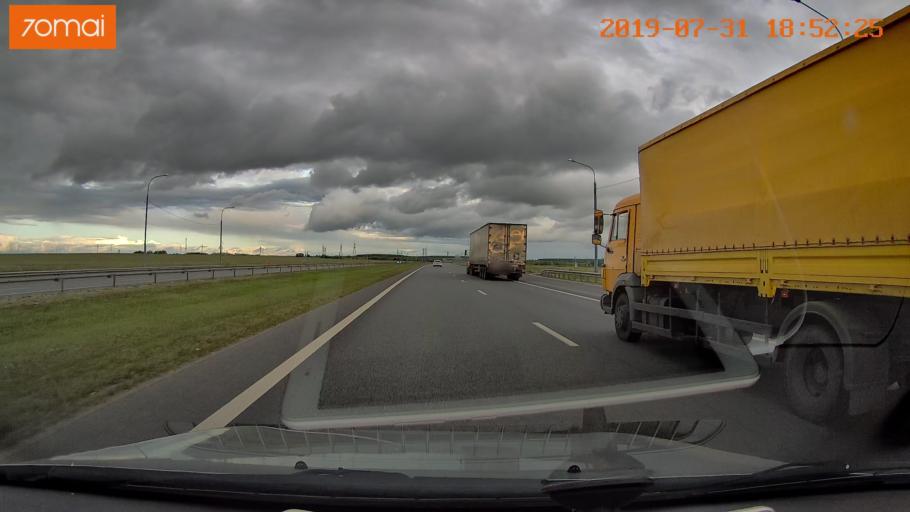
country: RU
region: Moskovskaya
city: Voskresensk
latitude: 55.2140
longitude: 38.6314
